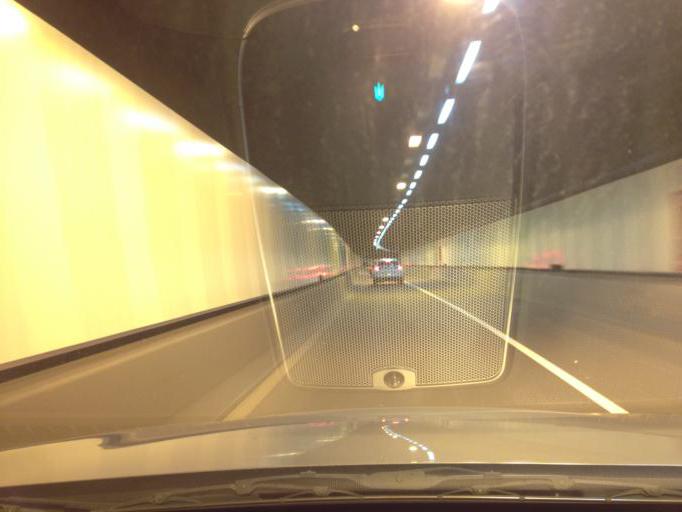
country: AU
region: New South Wales
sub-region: City of Sydney
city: Darlinghurst
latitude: -33.8851
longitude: 151.2181
